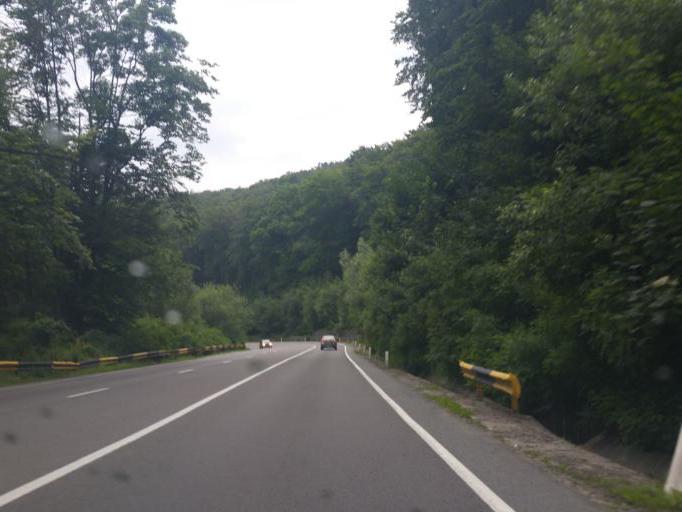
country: RO
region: Salaj
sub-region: Comuna Treznea
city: Treznea
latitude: 47.1501
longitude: 23.0917
